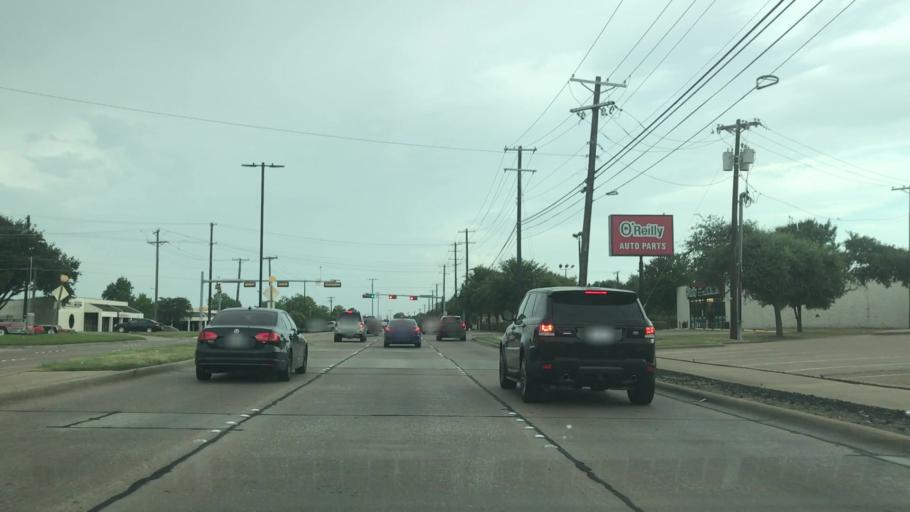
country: US
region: Texas
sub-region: Dallas County
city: Rowlett
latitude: 32.8628
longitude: -96.6036
